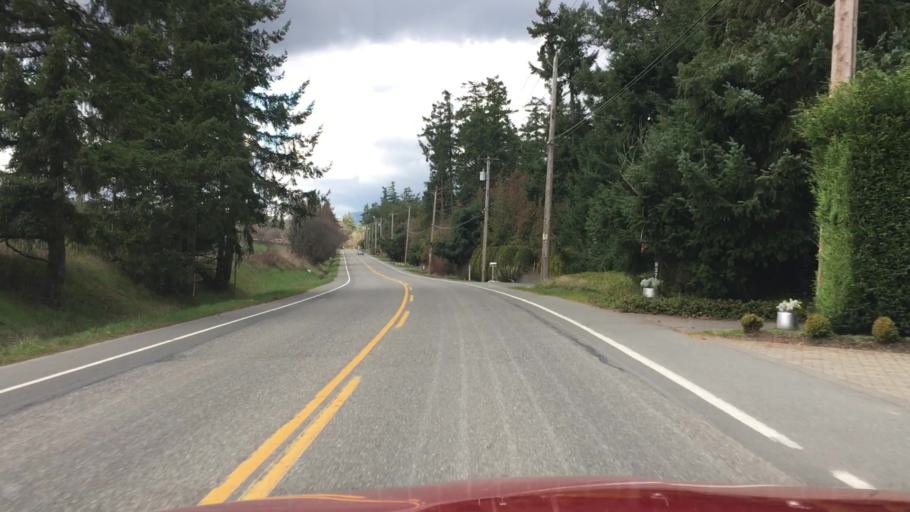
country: CA
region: British Columbia
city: North Saanich
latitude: 48.6066
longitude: -123.3965
